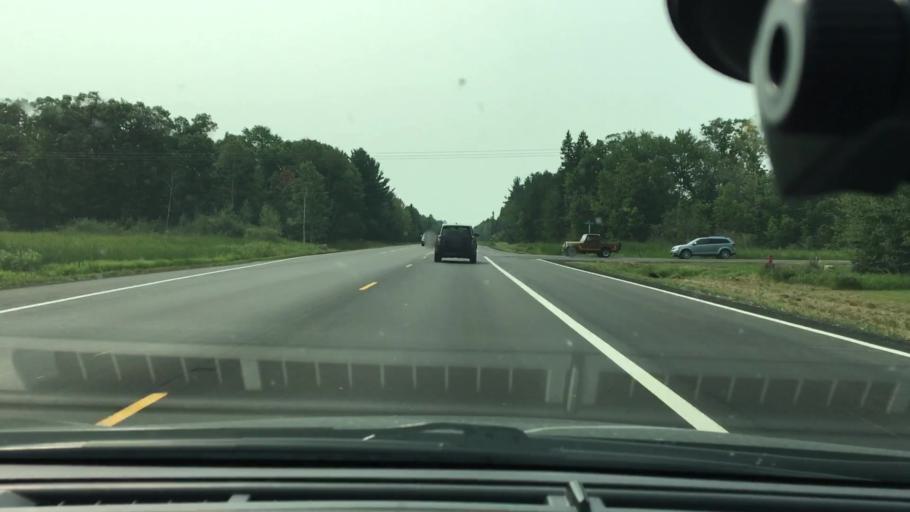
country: US
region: Minnesota
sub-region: Crow Wing County
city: Brainerd
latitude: 46.4505
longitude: -94.1721
